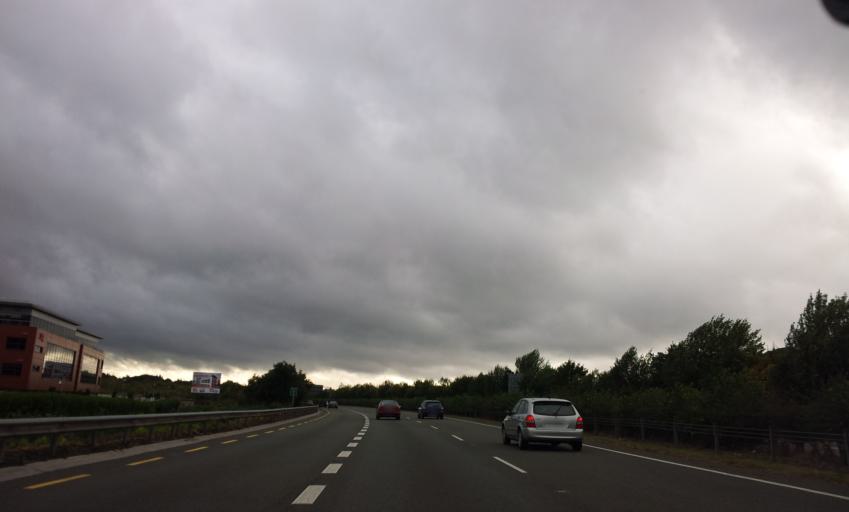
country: IE
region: Munster
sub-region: County Cork
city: Passage West
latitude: 51.9066
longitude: -8.3637
